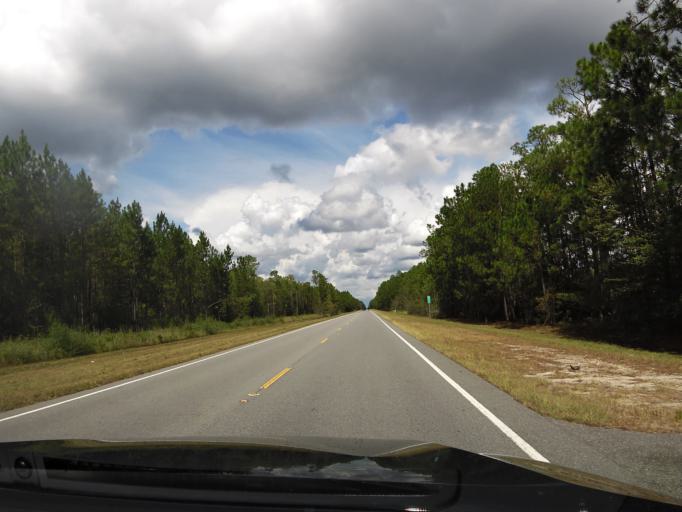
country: US
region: Georgia
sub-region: Charlton County
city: Folkston
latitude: 30.9301
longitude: -82.0216
